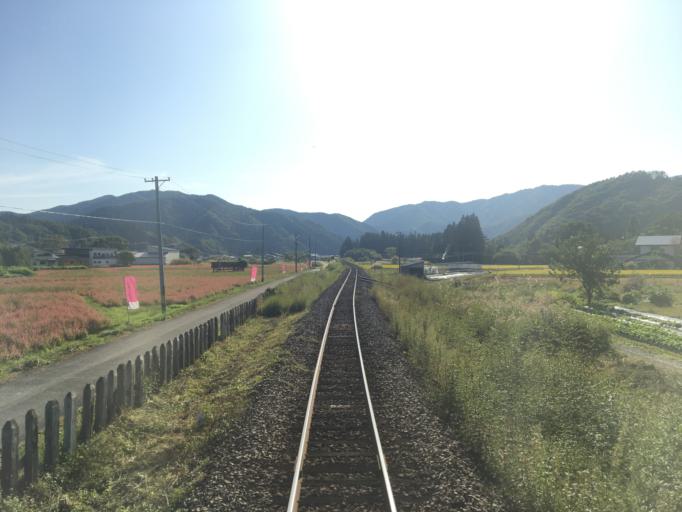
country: JP
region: Akita
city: Kakunodatemachi
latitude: 39.7438
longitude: 140.5901
